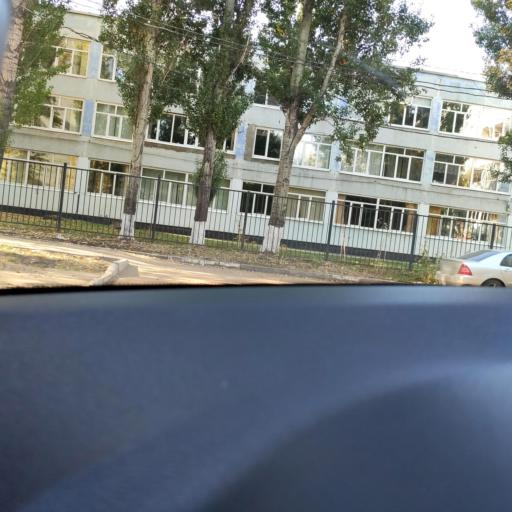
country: RU
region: Samara
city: Samara
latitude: 53.2070
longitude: 50.1433
